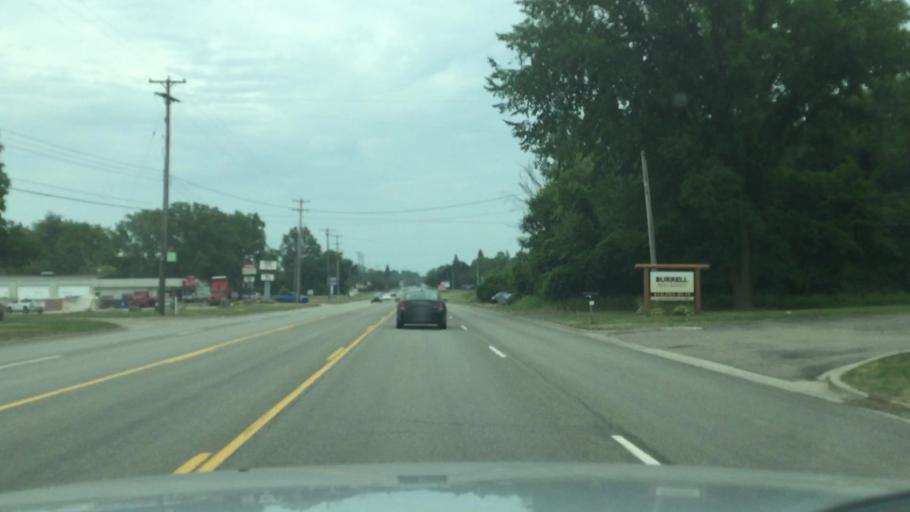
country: US
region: Michigan
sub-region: Genesee County
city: Flint
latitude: 42.9443
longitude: -83.7079
